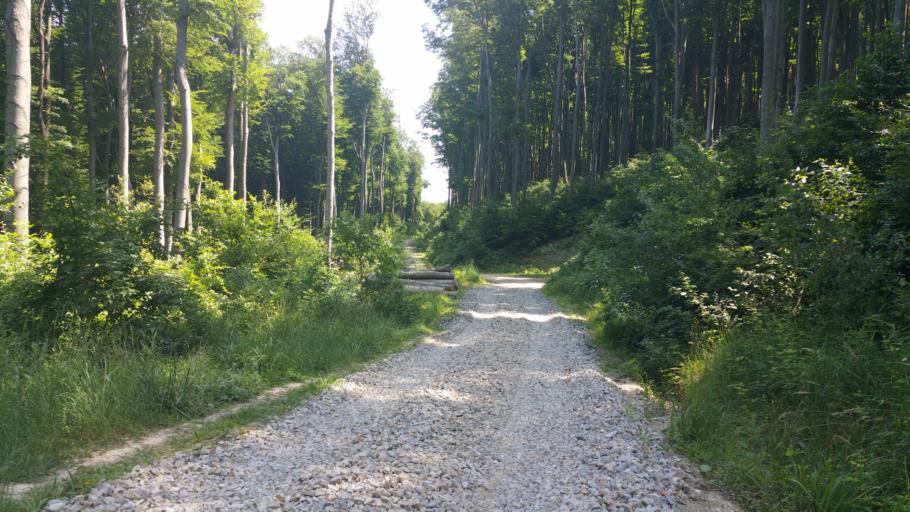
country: AT
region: Lower Austria
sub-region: Politischer Bezirk Wien-Umgebung
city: Klosterneuburg
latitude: 48.2374
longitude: 16.2727
